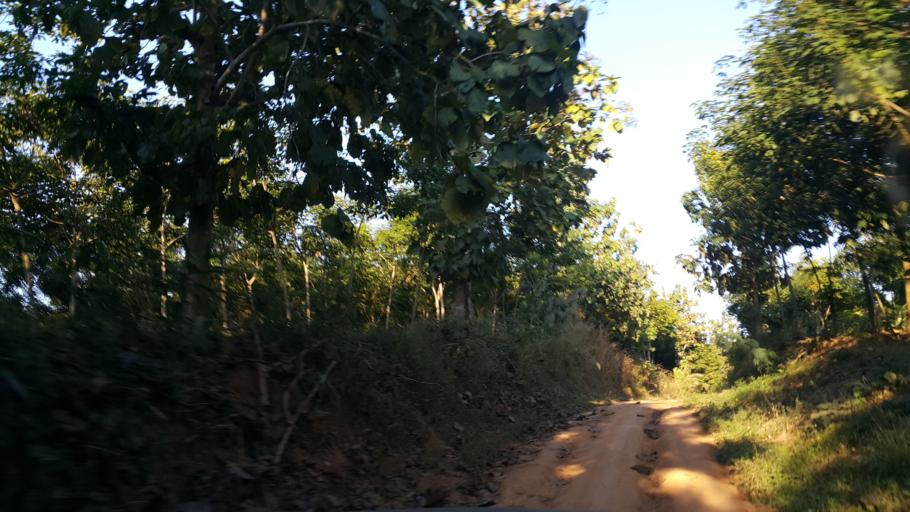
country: TH
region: Sukhothai
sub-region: Amphoe Si Satchanalai
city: Si Satchanalai
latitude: 17.5866
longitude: 99.6103
